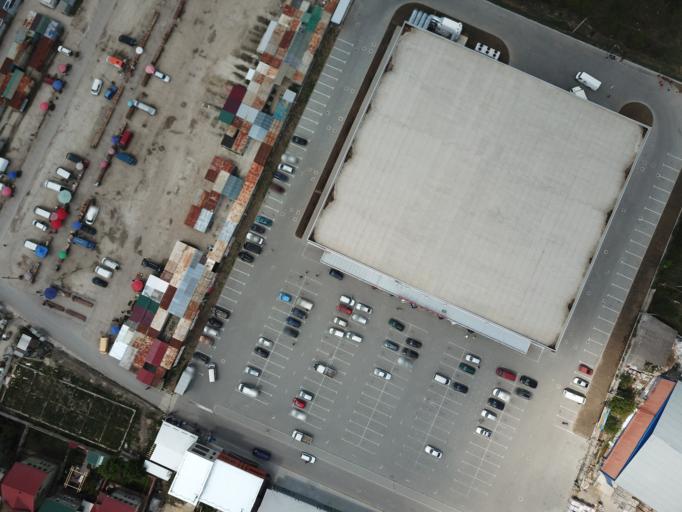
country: MD
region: Ungheni
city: Ungheni
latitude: 47.2120
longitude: 27.7954
